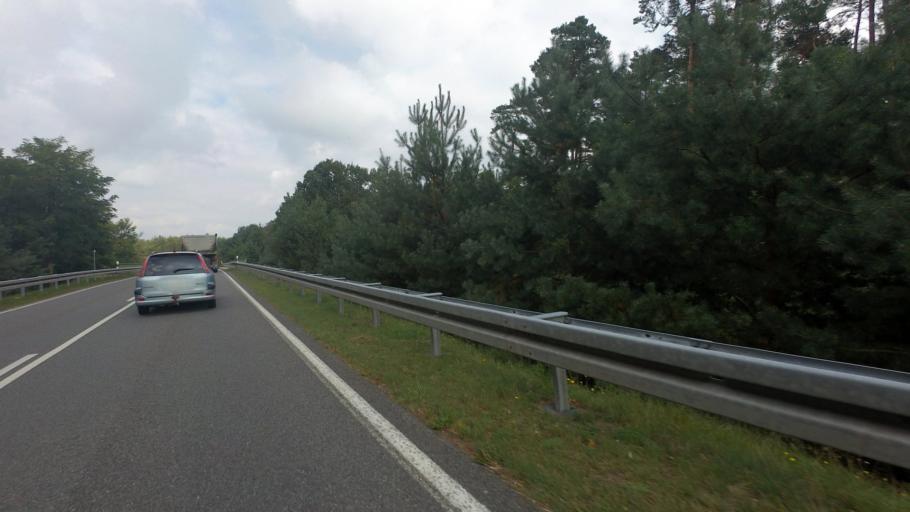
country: DE
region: Brandenburg
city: Bad Liebenwerda
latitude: 51.5303
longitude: 13.4112
